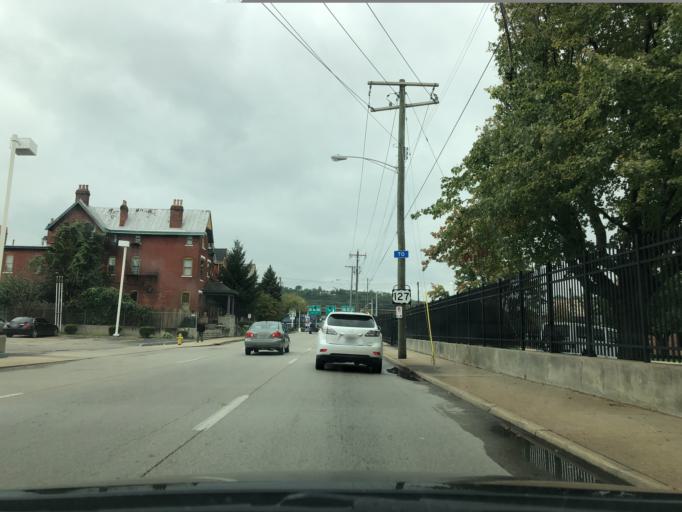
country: US
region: Kentucky
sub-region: Kenton County
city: Covington
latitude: 39.0866
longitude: -84.5144
